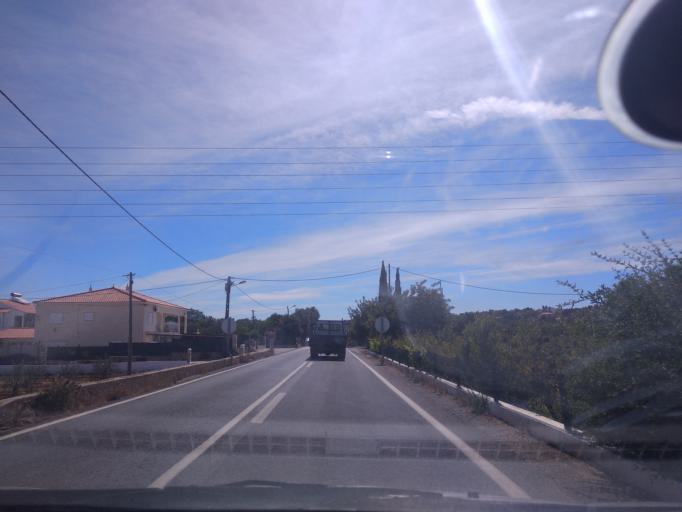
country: PT
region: Faro
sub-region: Sao Bras de Alportel
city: Sao Bras de Alportel
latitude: 37.1547
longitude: -7.8596
